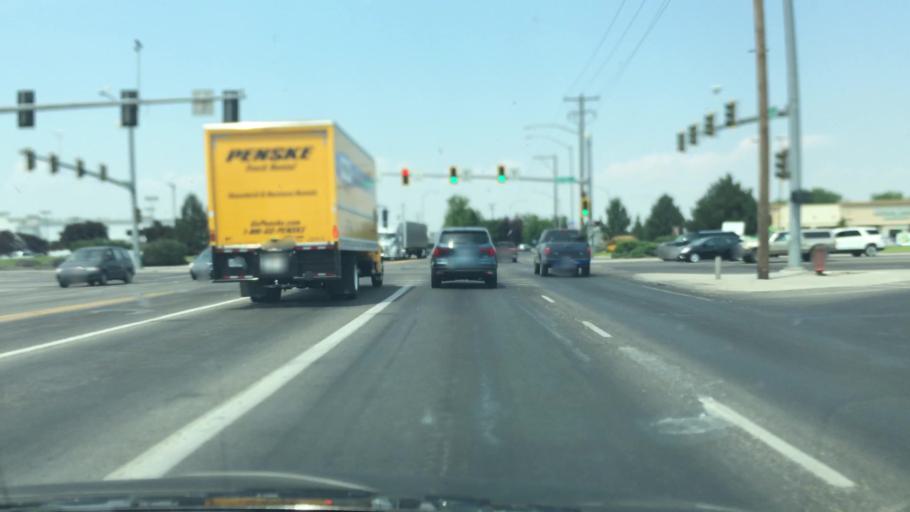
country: US
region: Idaho
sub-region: Twin Falls County
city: Twin Falls
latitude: 42.5915
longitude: -114.4601
